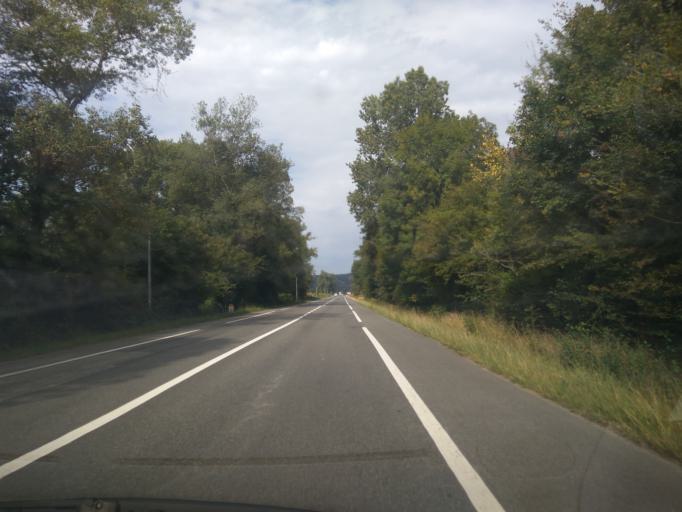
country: FR
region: Aquitaine
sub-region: Departement des Pyrenees-Atlantiques
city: Arbus
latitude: 43.3309
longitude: -0.4845
